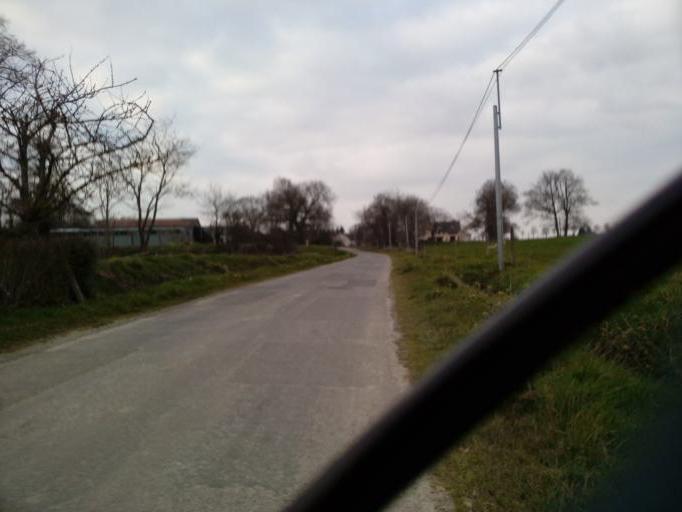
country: FR
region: Brittany
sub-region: Departement d'Ille-et-Vilaine
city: Talensac
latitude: 48.1125
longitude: -1.9029
